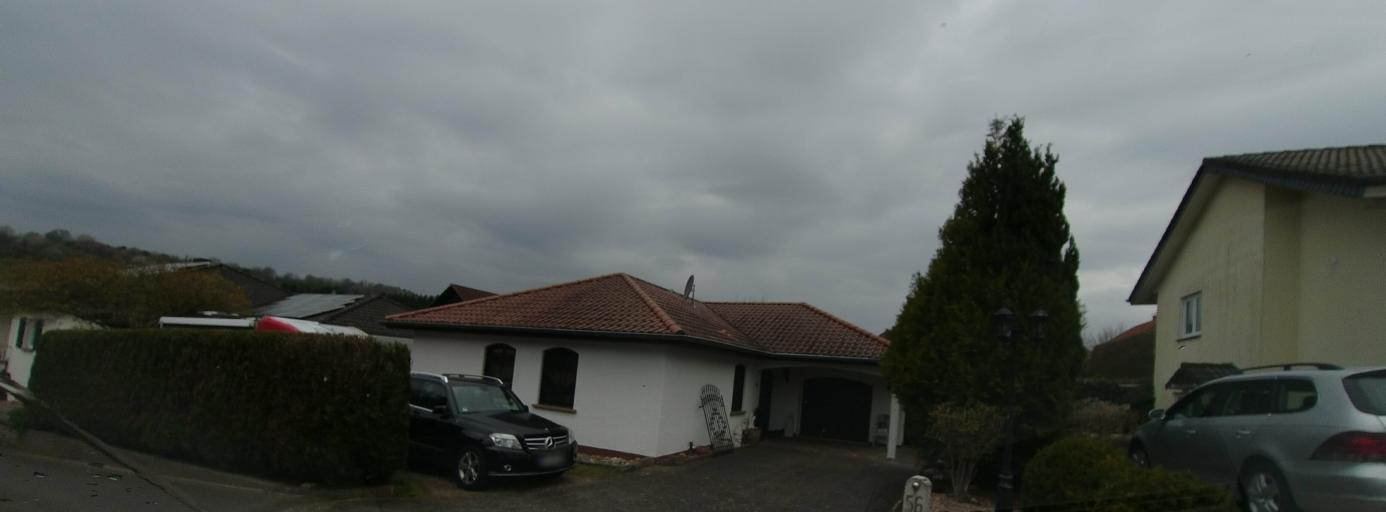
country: DE
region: Saarland
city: Losheim
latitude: 49.5000
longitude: 6.7725
